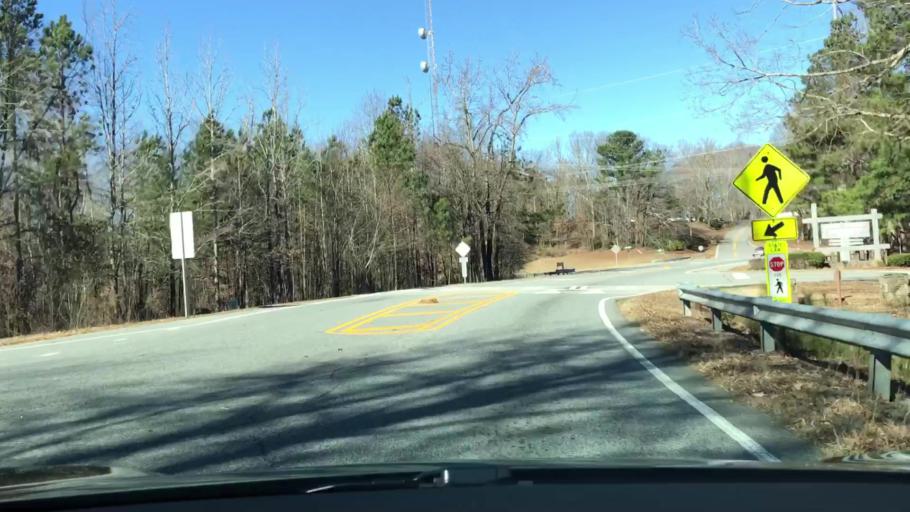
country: US
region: Georgia
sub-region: Gwinnett County
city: Sugar Hill
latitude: 34.1544
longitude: -84.0707
